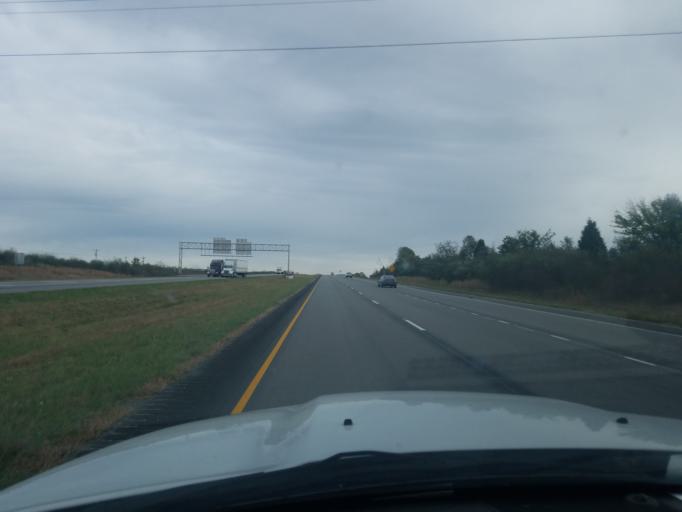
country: US
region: Indiana
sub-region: Spencer County
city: Dale
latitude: 38.1936
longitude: -86.9746
